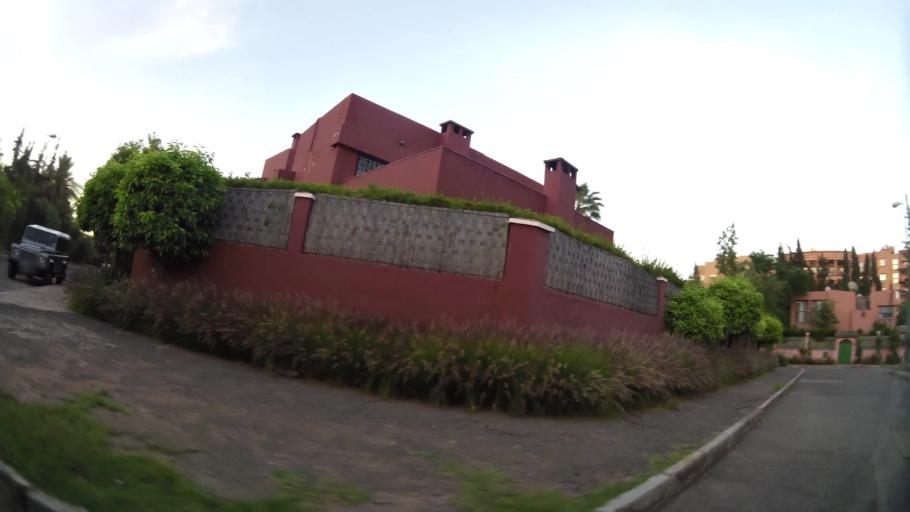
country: MA
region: Marrakech-Tensift-Al Haouz
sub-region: Marrakech
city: Marrakesh
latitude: 31.6438
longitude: -8.0228
